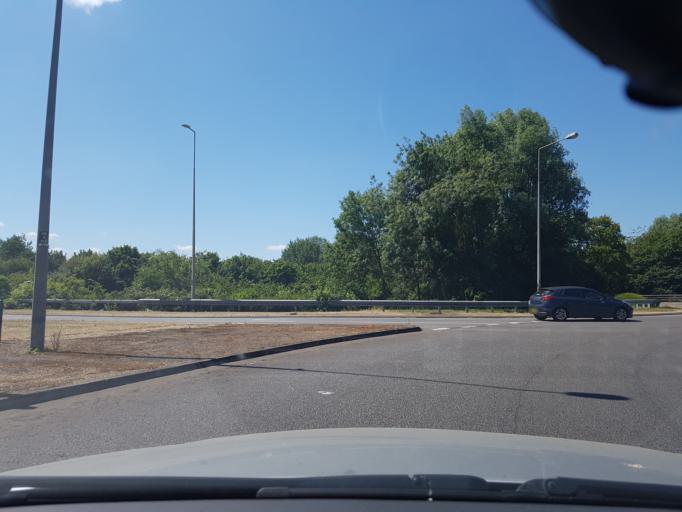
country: GB
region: England
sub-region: Milton Keynes
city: Bradwell
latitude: 52.0457
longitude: -0.7789
